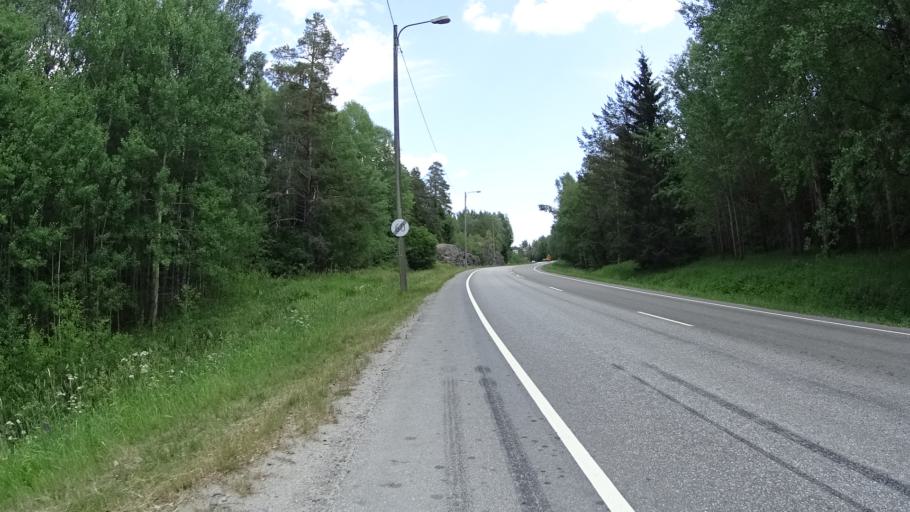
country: FI
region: Uusimaa
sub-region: Raaseporin
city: Pohja
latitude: 60.1042
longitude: 23.5630
